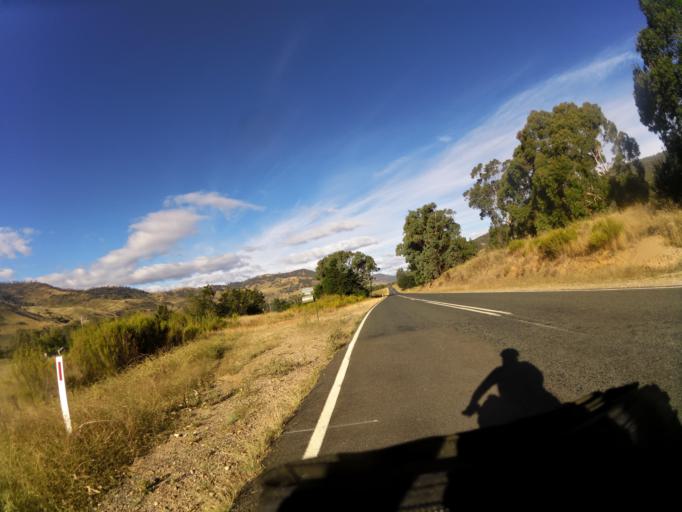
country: AU
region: New South Wales
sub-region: Greater Hume Shire
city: Holbrook
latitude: -35.9708
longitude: 147.7868
